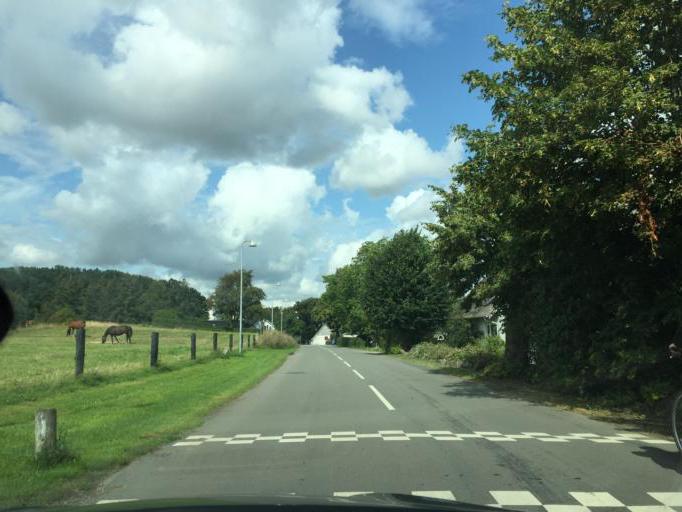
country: DK
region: South Denmark
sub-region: Odense Kommune
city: Stige
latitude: 55.4610
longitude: 10.3767
